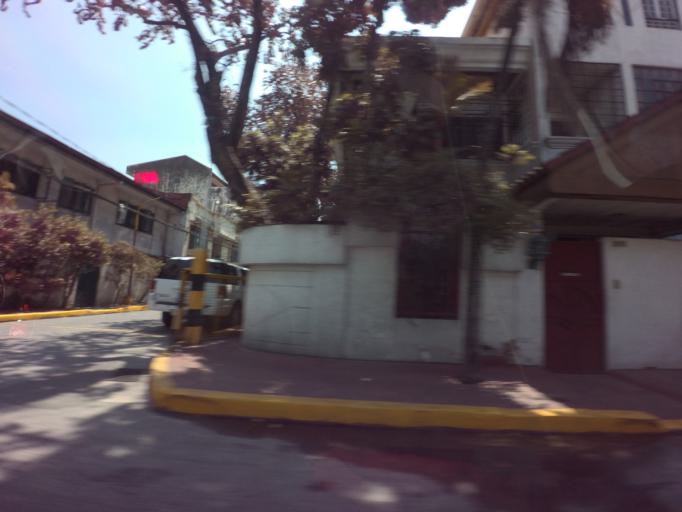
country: PH
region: Metro Manila
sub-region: Makati City
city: Makati City
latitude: 14.5650
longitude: 120.9989
